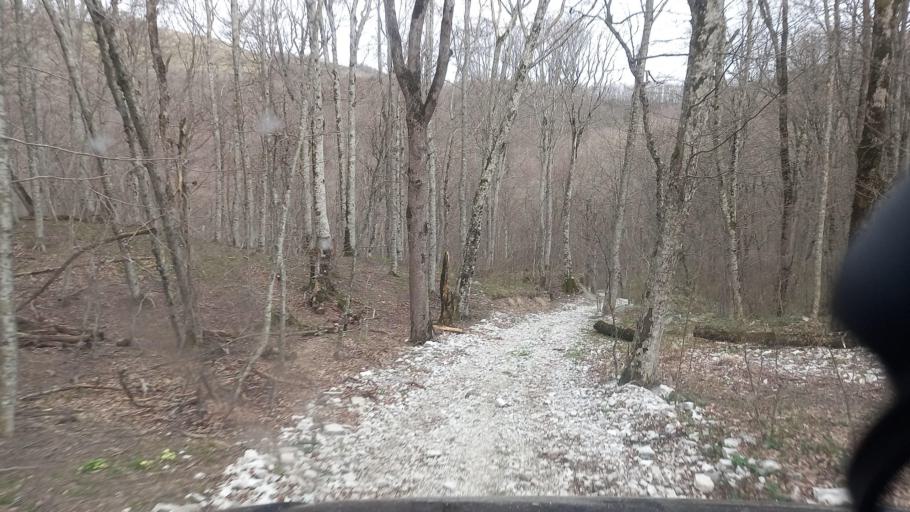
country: RU
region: Krasnodarskiy
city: Gelendzhik
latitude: 44.6171
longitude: 38.2030
